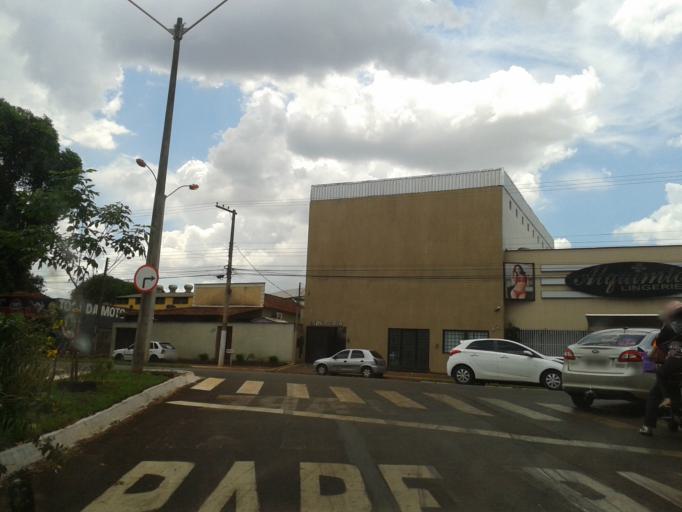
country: BR
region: Goias
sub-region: Itumbiara
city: Itumbiara
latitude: -18.4104
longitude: -49.2110
